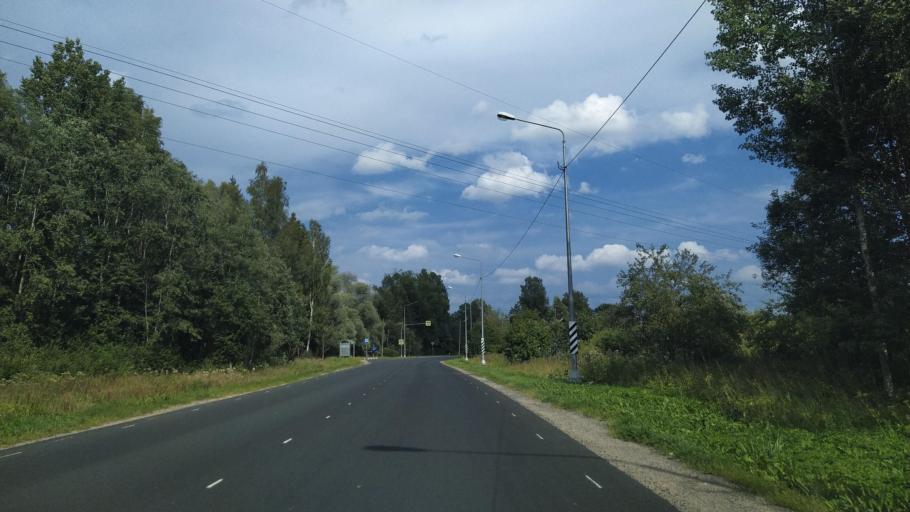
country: RU
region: Pskov
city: Vybor
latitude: 57.7308
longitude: 28.9732
